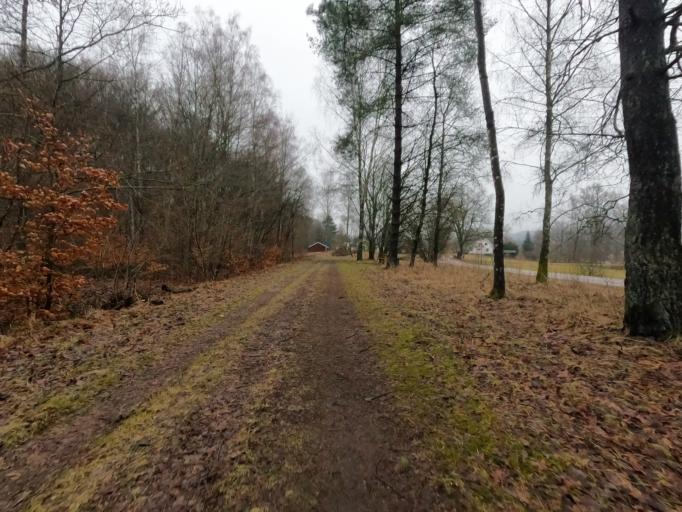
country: SE
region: Halland
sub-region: Halmstads Kommun
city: Oskarstrom
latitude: 56.7497
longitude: 13.1690
